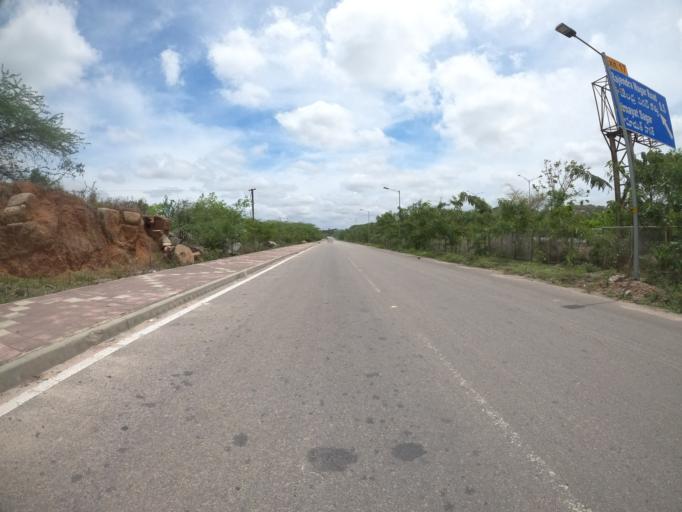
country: IN
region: Telangana
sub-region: Hyderabad
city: Hyderabad
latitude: 17.3009
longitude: 78.3787
